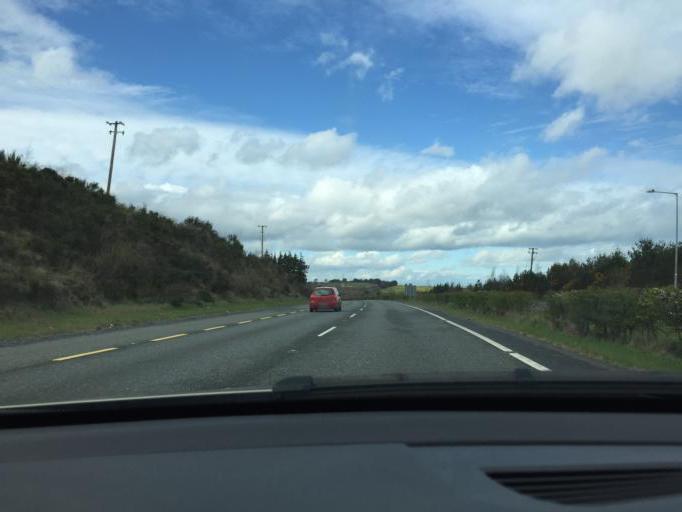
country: IE
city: Newtownmountkennedy
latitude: 53.0654
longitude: -6.0920
